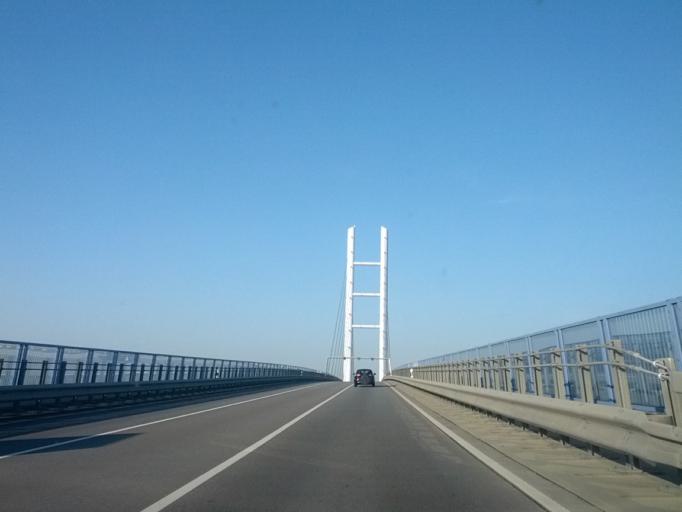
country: DE
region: Mecklenburg-Vorpommern
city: Altefahr
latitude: 54.3096
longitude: 13.1140
